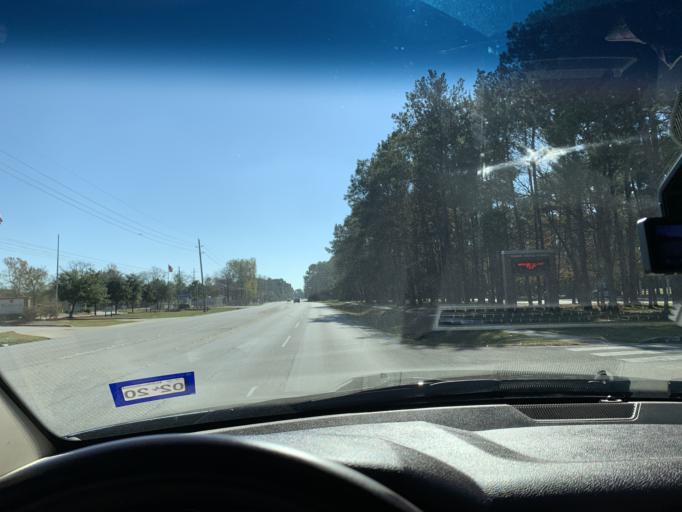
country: US
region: Texas
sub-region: Harris County
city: Spring
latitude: 30.0040
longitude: -95.4436
